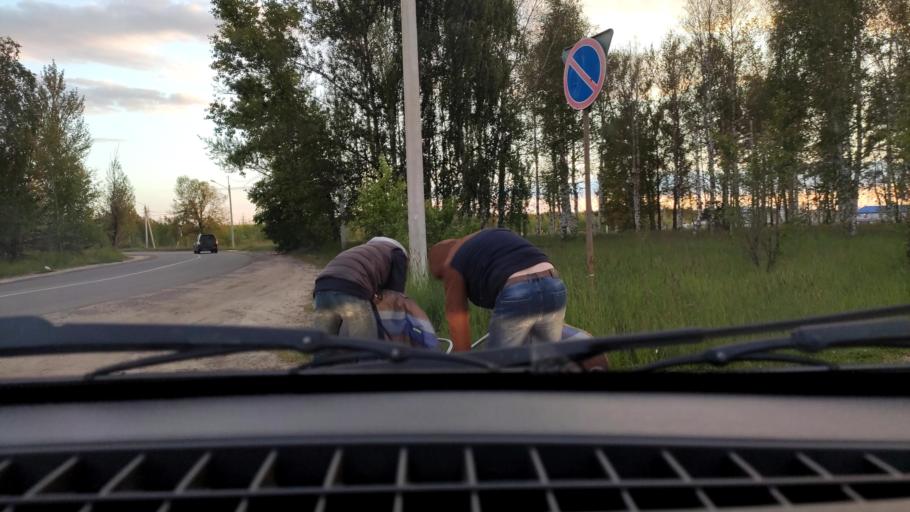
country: RU
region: Voronezj
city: Somovo
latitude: 51.7320
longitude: 39.3206
